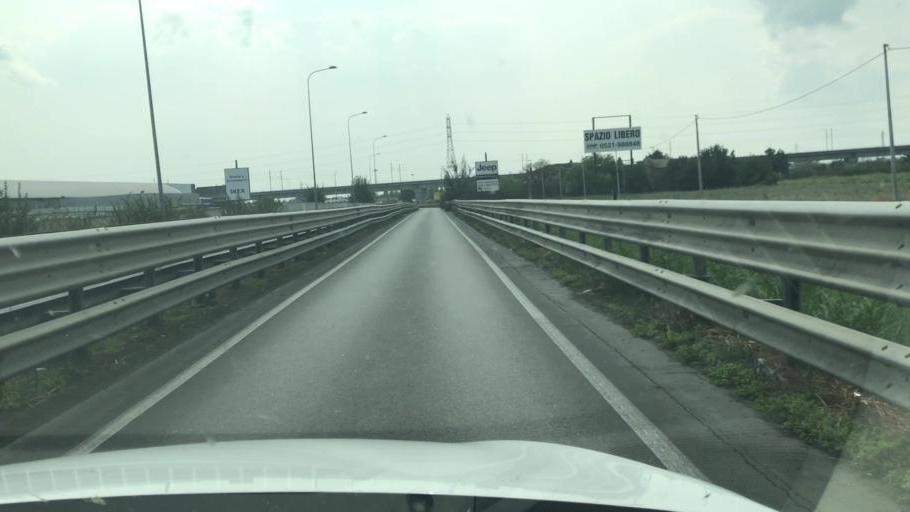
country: IT
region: Emilia-Romagna
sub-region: Provincia di Parma
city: Baganzola
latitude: 44.8449
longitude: 10.3406
